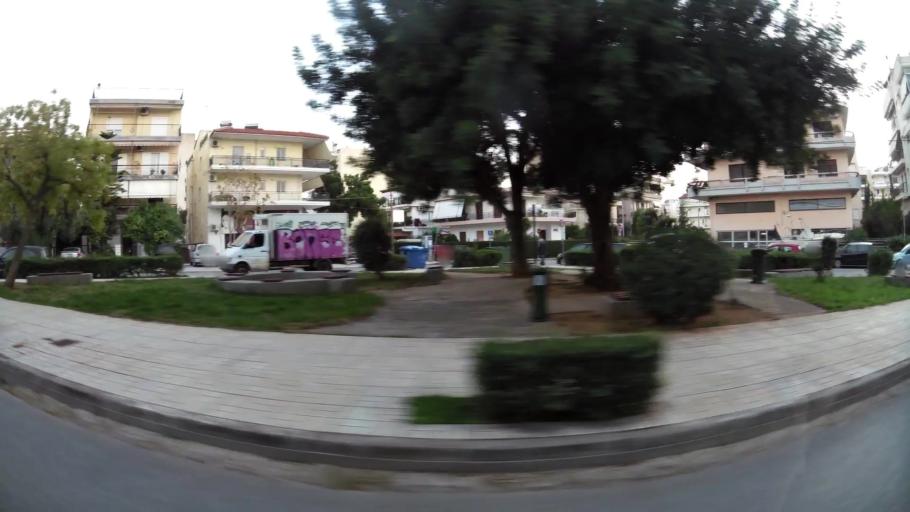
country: GR
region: Attica
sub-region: Nomarchia Athinas
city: Argyroupoli
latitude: 37.8893
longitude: 23.7566
